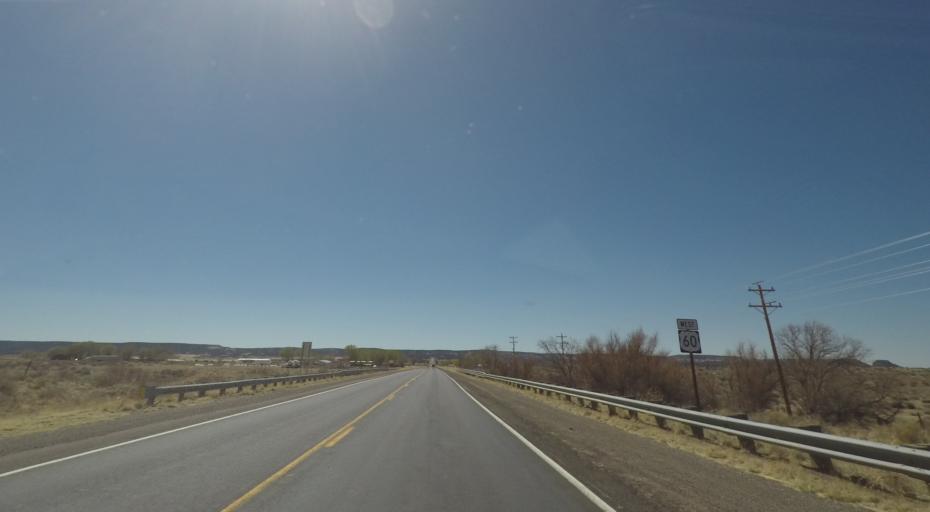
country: US
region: New Mexico
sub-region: Catron County
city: Reserve
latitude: 34.3440
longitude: -108.5059
